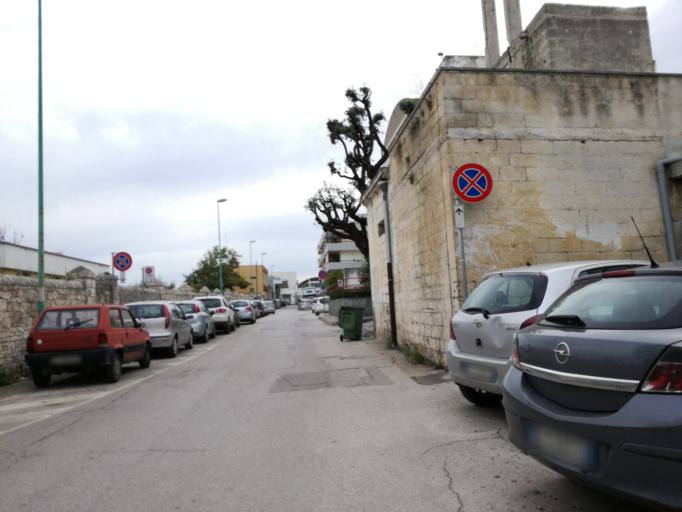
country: IT
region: Apulia
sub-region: Provincia di Bari
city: Adelfia
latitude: 41.0026
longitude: 16.8717
